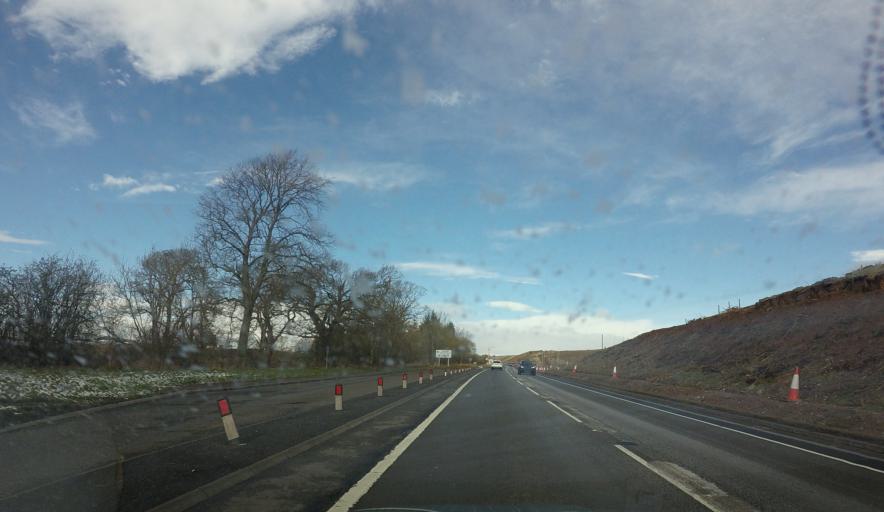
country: GB
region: Scotland
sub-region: Perth and Kinross
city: Bankfoot
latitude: 56.4848
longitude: -3.4991
